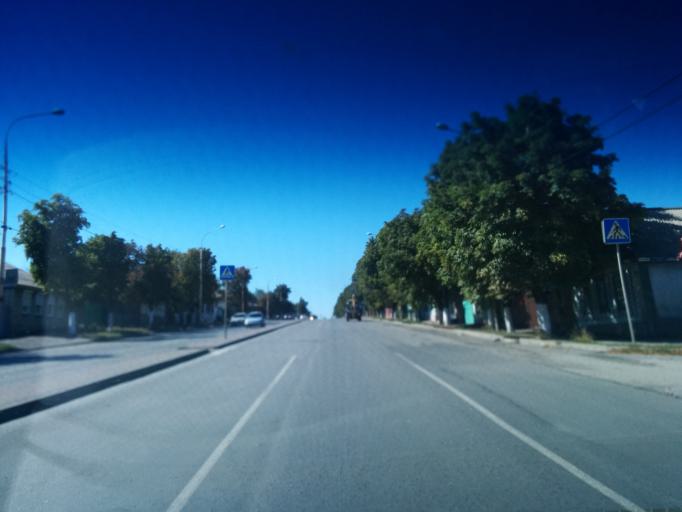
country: RU
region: Rostov
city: Shakhty
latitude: 47.7002
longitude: 40.2335
